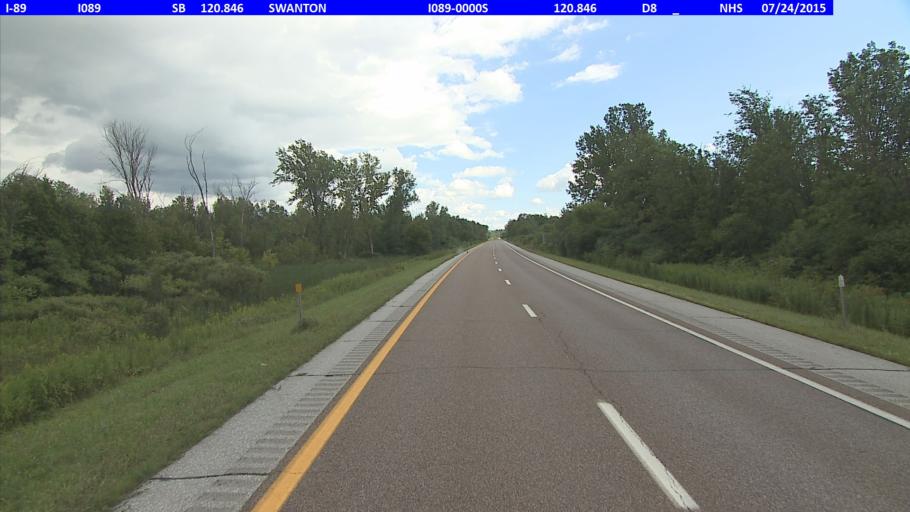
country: US
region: Vermont
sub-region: Franklin County
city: Swanton
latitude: 44.8893
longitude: -73.0870
